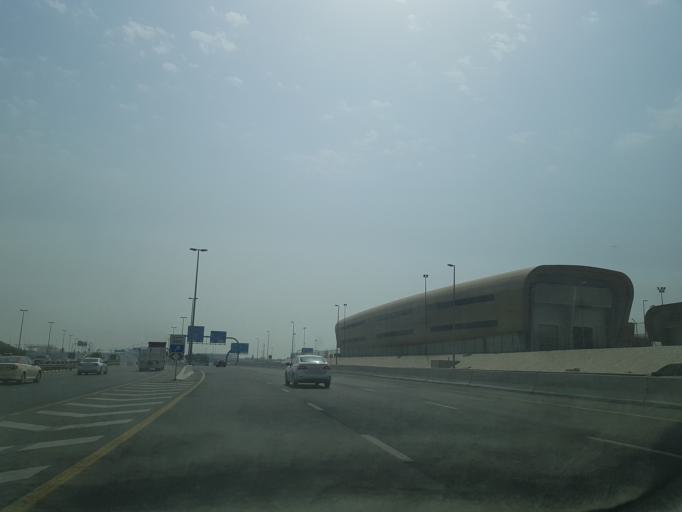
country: AE
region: Ash Shariqah
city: Sharjah
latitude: 25.2305
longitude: 55.3989
